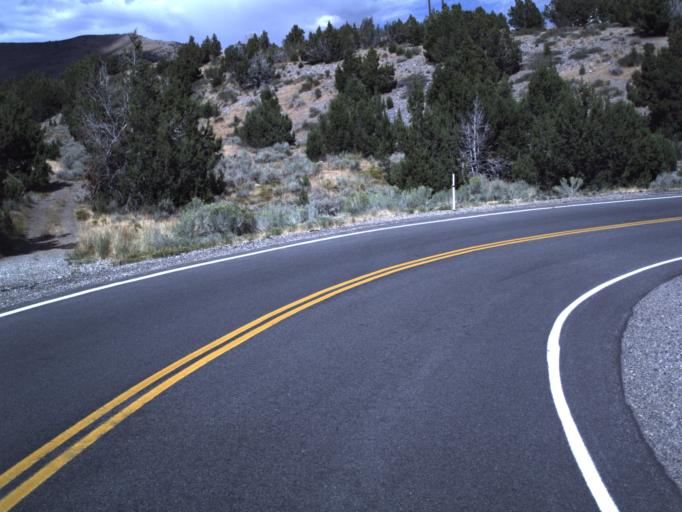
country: US
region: Utah
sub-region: Tooele County
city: Grantsville
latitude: 40.3489
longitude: -112.5517
